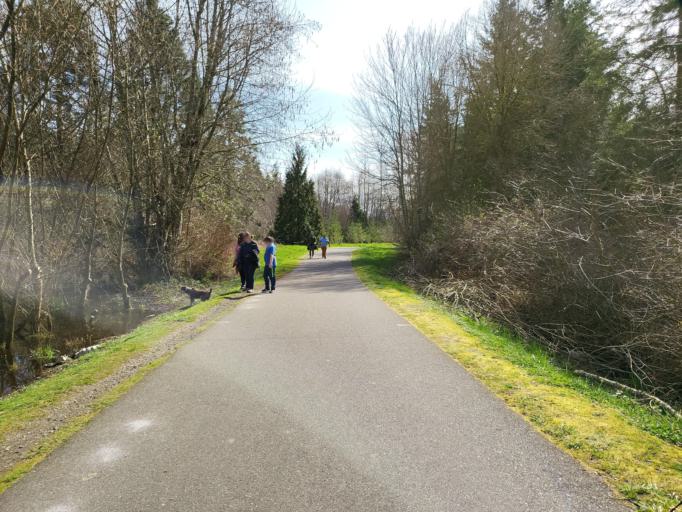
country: US
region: Washington
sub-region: King County
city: East Hill-Meridian
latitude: 47.4148
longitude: -122.1584
